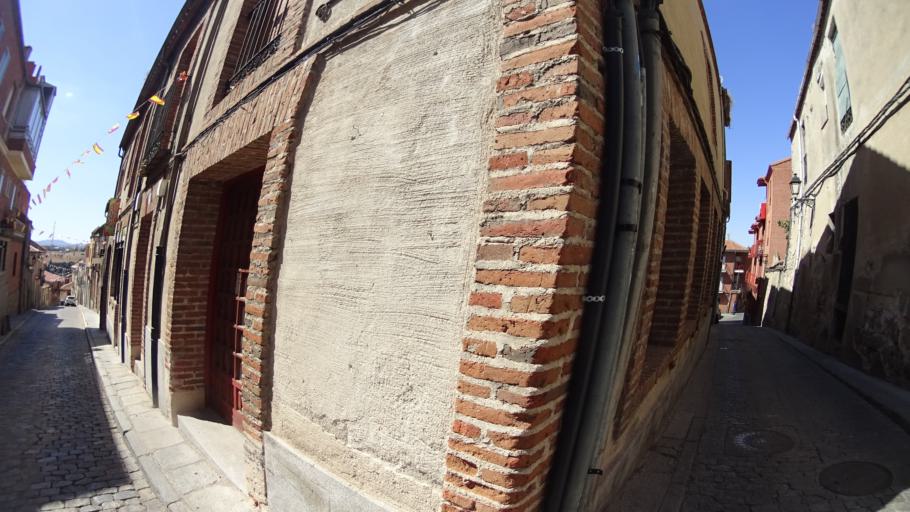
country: ES
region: Castille and Leon
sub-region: Provincia de Avila
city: Avila
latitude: 40.6569
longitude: -4.7030
